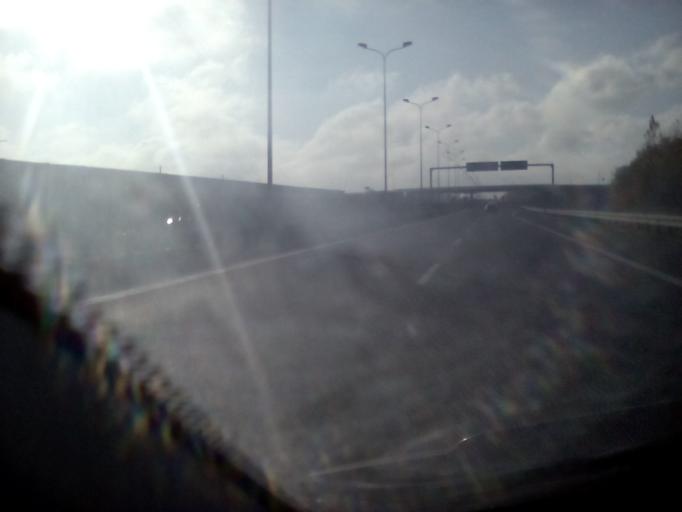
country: PL
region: Masovian Voivodeship
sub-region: Powiat grojecki
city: Goszczyn
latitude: 51.7628
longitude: 20.9030
